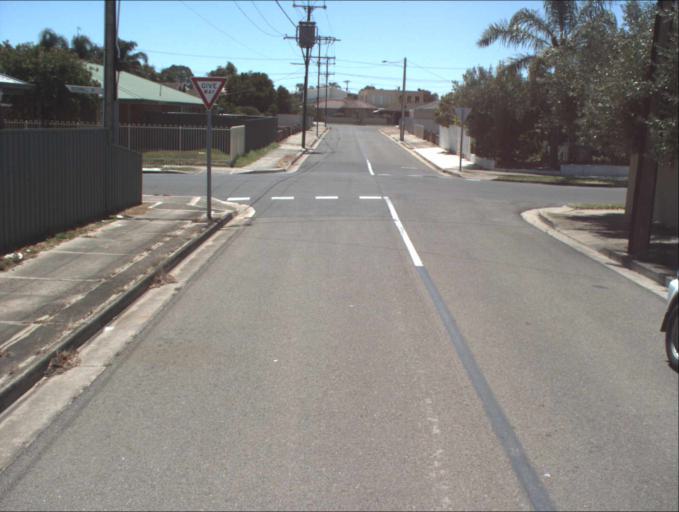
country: AU
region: South Australia
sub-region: Port Adelaide Enfield
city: Birkenhead
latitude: -34.8435
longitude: 138.4911
